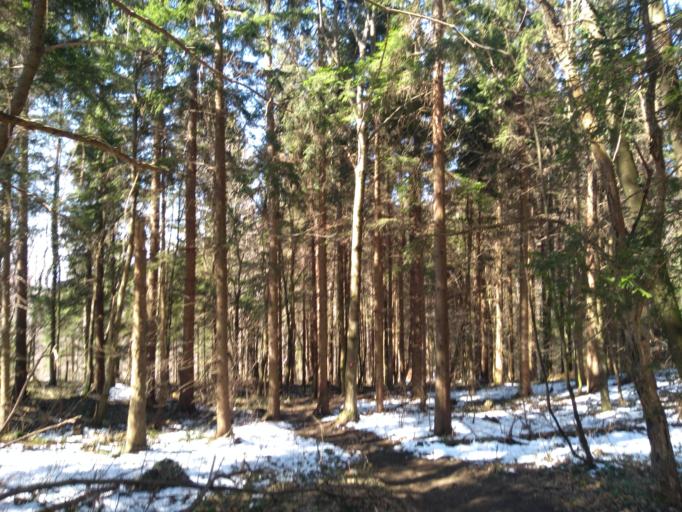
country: HR
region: Varazdinska
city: Ivanec
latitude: 46.1826
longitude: 16.1108
